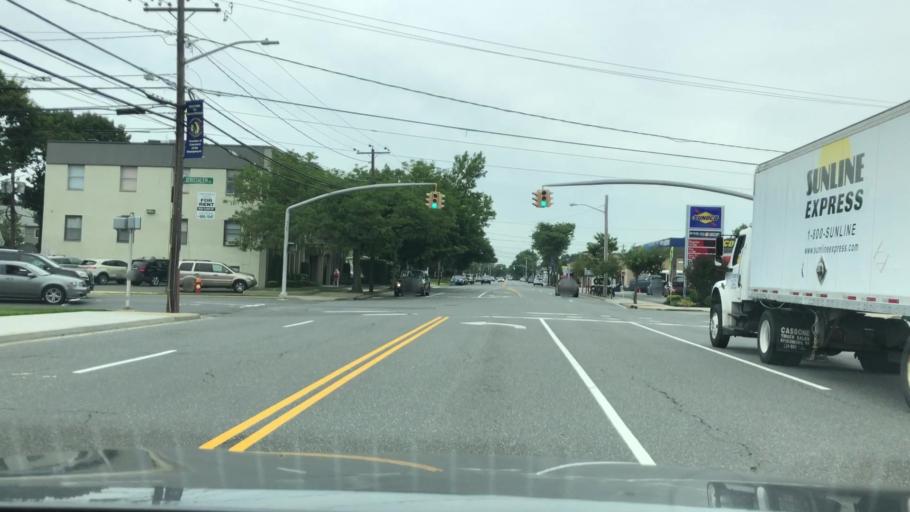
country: US
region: New York
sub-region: Nassau County
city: North Massapequa
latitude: 40.6921
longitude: -73.4652
